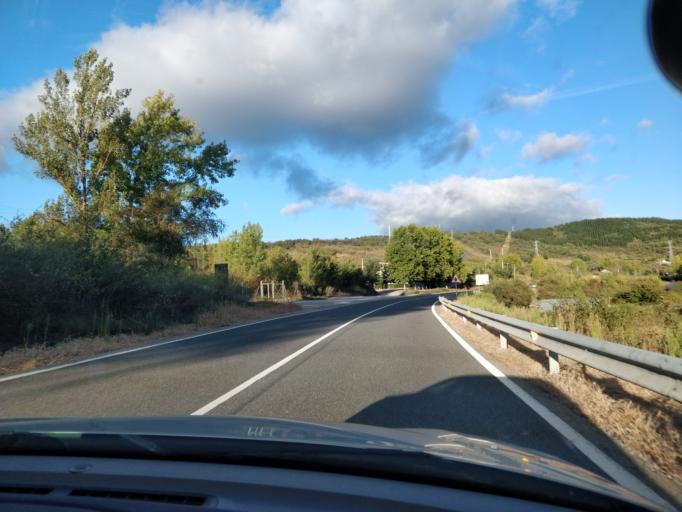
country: ES
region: Castille and Leon
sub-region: Provincia de Leon
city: Borrenes
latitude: 42.4997
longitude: -6.7302
